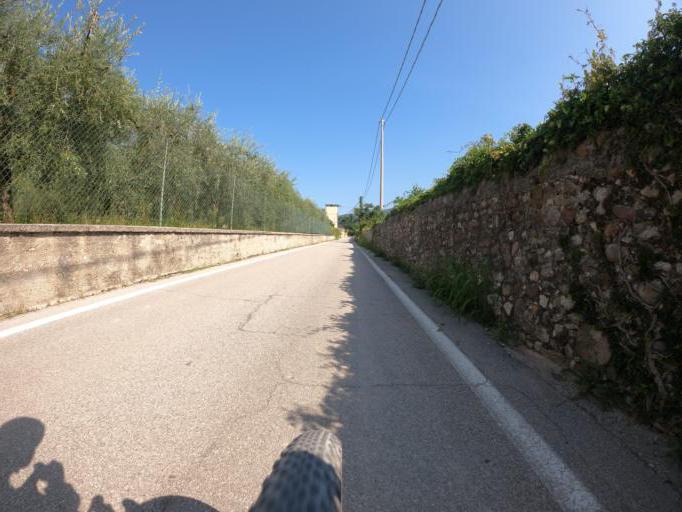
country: IT
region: Veneto
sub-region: Provincia di Verona
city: Costermano
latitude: 45.5829
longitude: 10.7459
